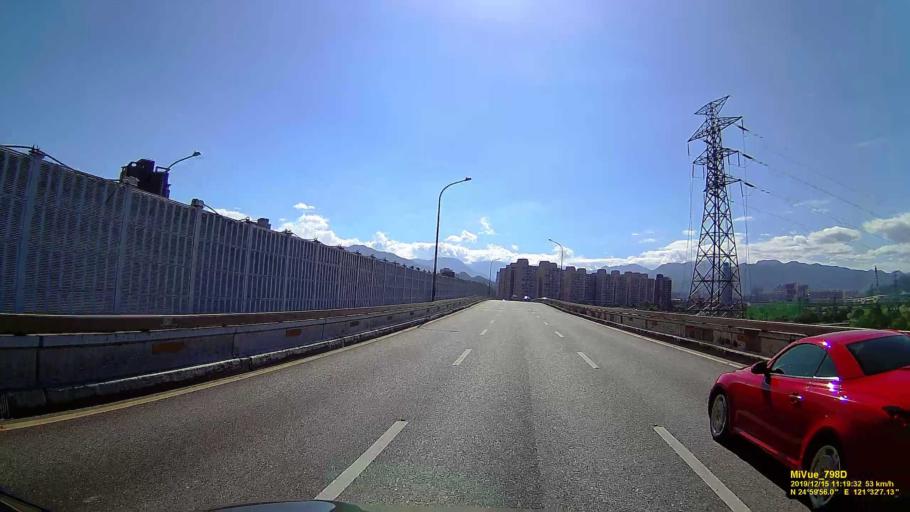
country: TW
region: Taipei
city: Taipei
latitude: 24.9994
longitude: 121.5364
